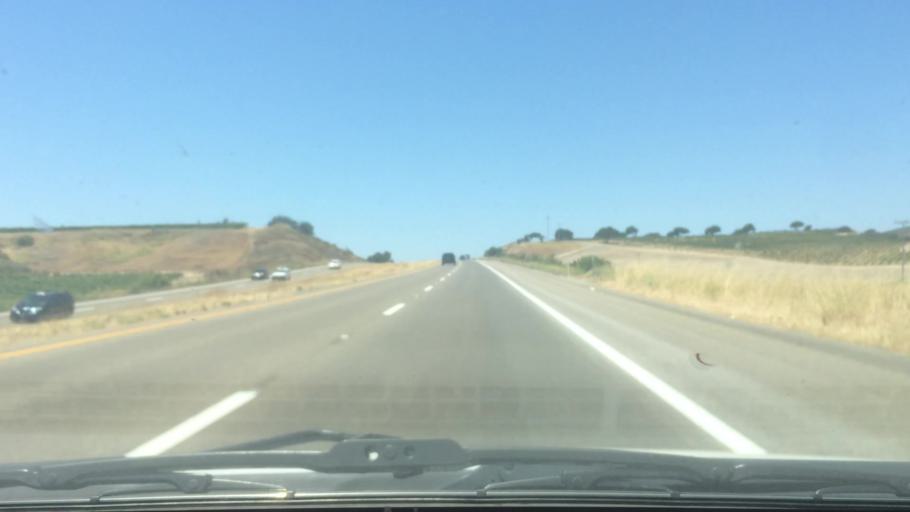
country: US
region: California
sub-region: Santa Barbara County
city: Los Alamos
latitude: 34.7653
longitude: -120.3026
